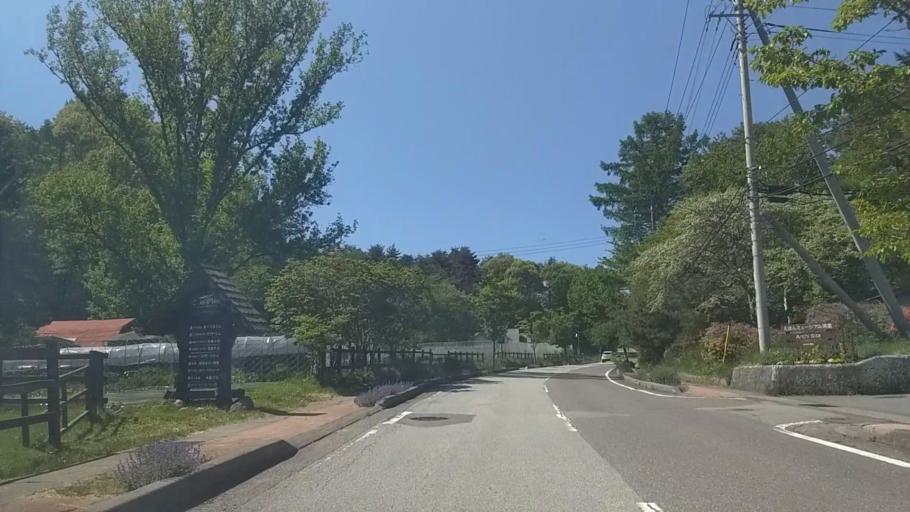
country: JP
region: Yamanashi
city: Nirasaki
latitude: 35.8969
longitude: 138.4375
